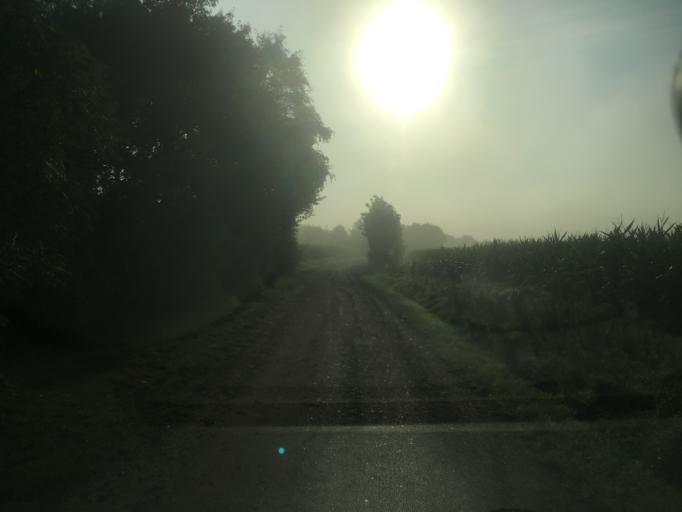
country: DK
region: South Denmark
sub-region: Tonder Kommune
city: Logumkloster
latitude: 55.0134
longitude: 8.9099
